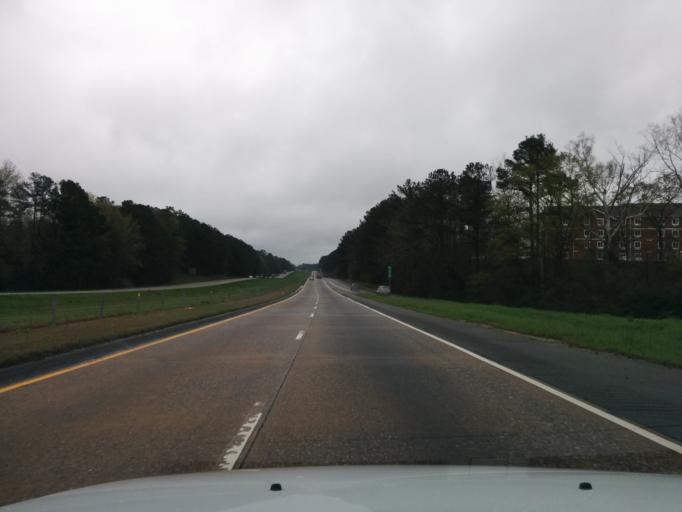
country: US
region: Georgia
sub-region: Bibb County
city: Macon
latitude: 32.9267
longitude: -83.7288
